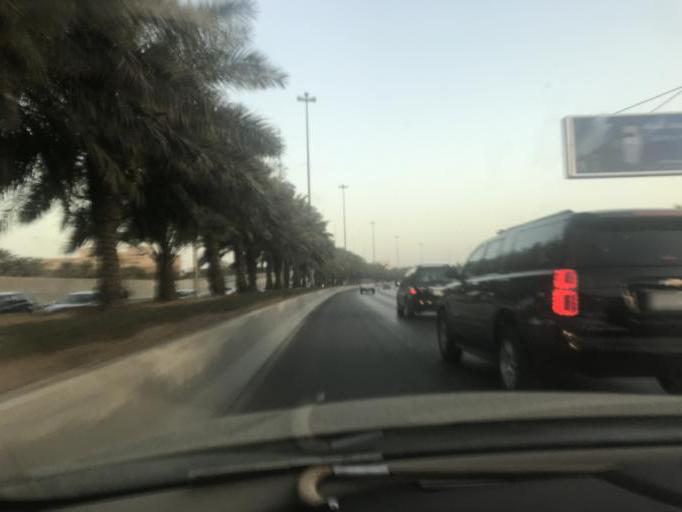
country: SA
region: Ar Riyad
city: Riyadh
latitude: 24.8103
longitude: 46.7139
